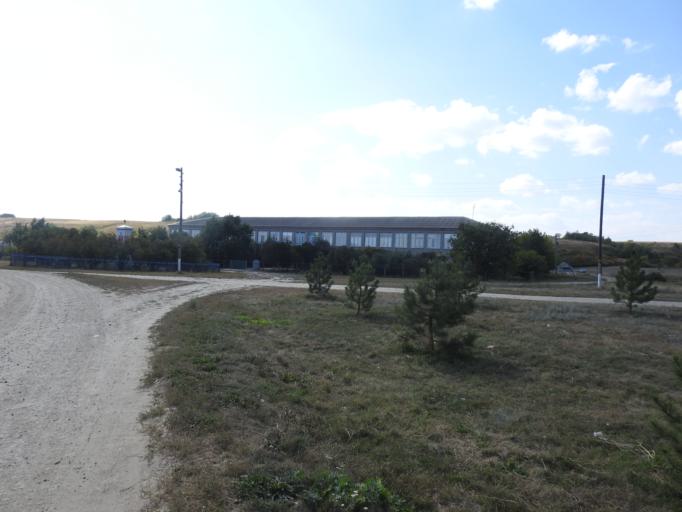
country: RU
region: Volgograd
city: Zhirnovsk
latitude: 51.2199
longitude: 44.9441
